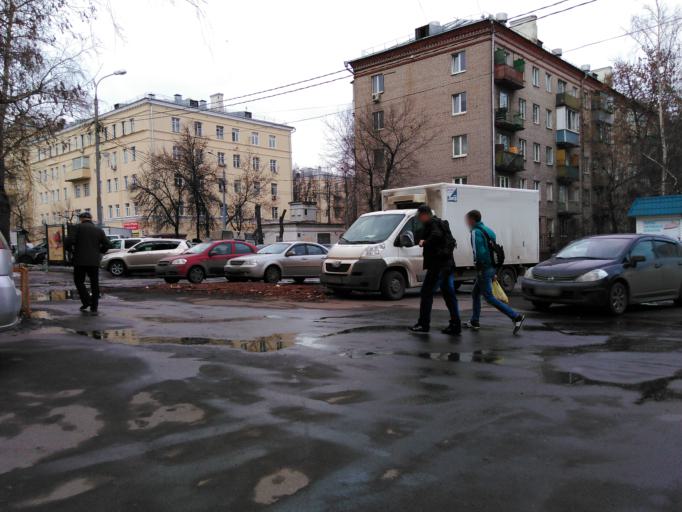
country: RU
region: Moscow
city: Vatutino
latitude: 55.8636
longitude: 37.6817
